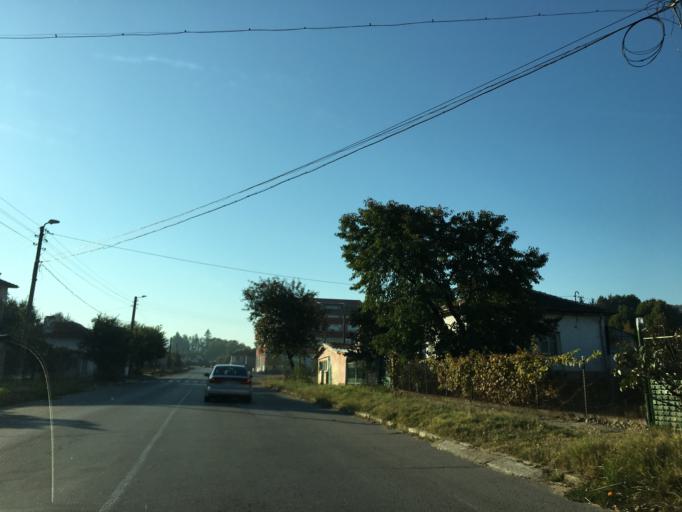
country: BG
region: Sofiya
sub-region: Obshtina Ikhtiman
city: Ikhtiman
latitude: 42.3887
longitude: 23.8720
